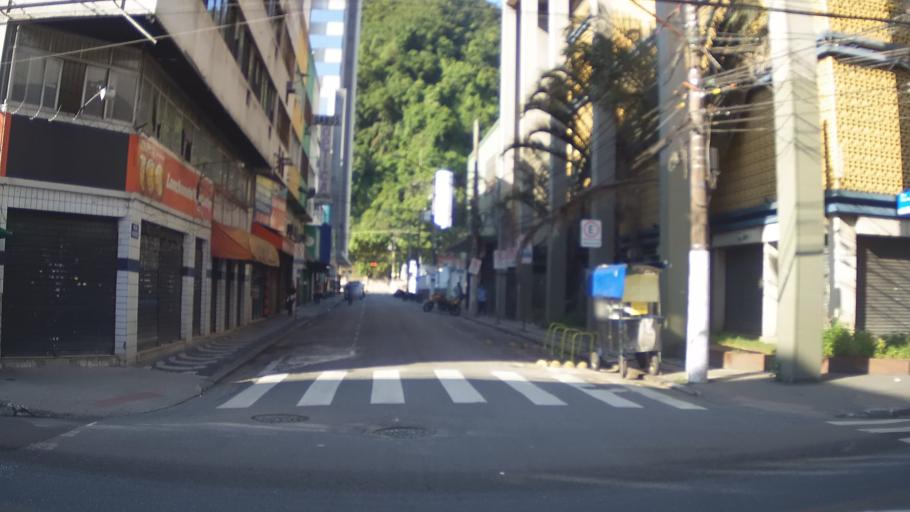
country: BR
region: Sao Paulo
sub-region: Santos
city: Santos
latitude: -23.9355
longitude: -46.3295
